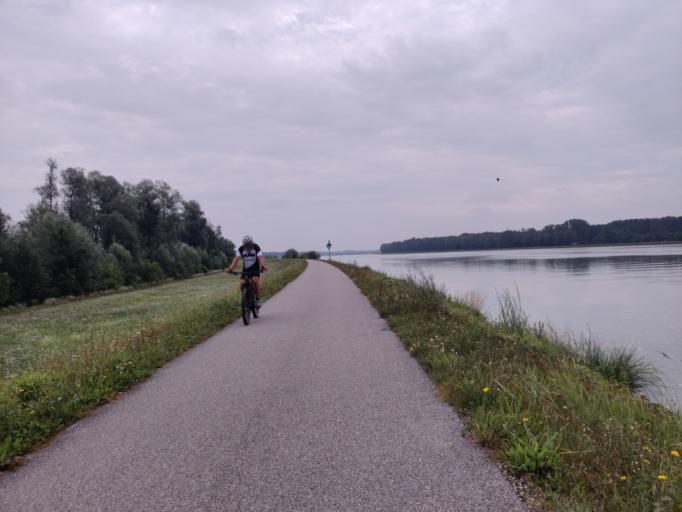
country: AT
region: Upper Austria
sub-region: Politischer Bezirk Urfahr-Umgebung
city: Steyregg
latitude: 48.2589
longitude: 14.4026
